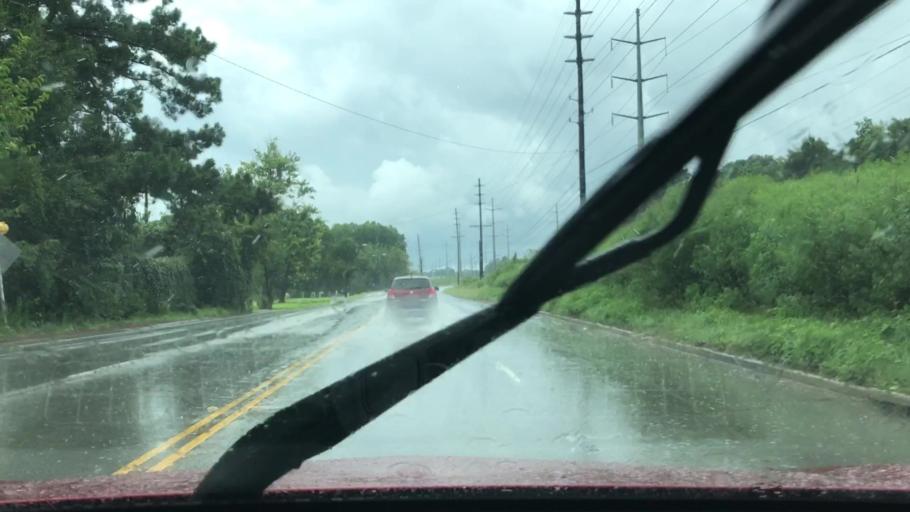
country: US
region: South Carolina
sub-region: Charleston County
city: North Charleston
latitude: 32.8469
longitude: -79.9903
